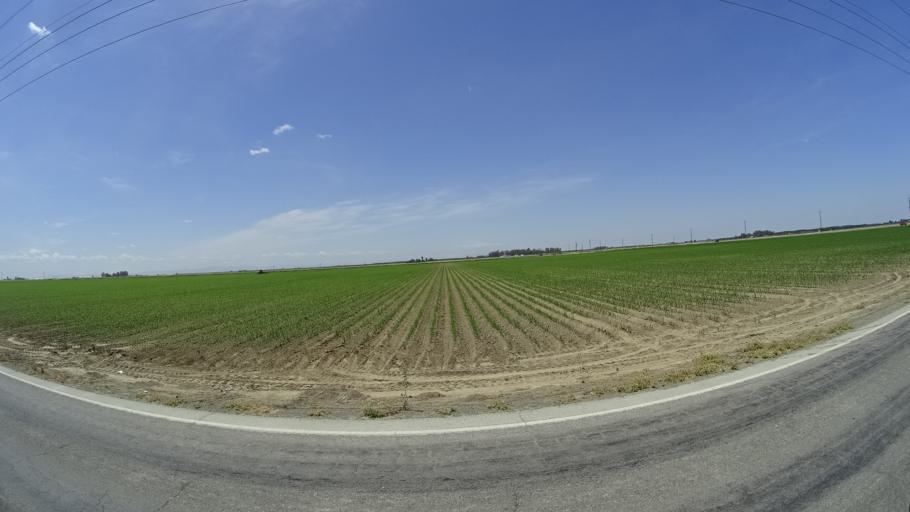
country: US
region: California
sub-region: Kings County
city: Home Garden
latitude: 36.2524
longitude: -119.6549
